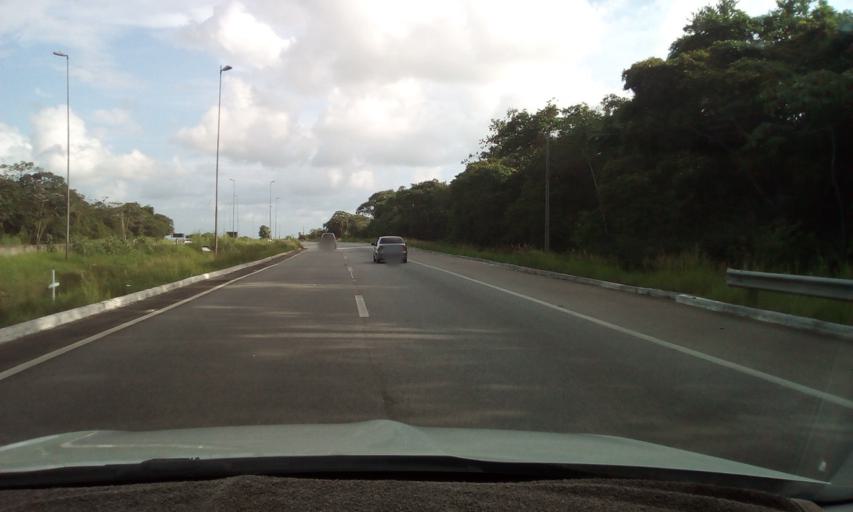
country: BR
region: Paraiba
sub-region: Mamanguape
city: Mamanguape
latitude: -6.8783
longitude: -35.1320
